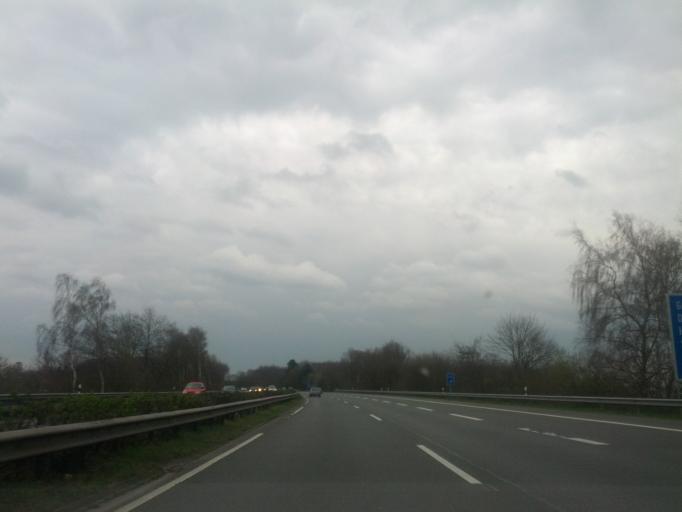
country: DE
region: Lower Saxony
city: Ganderkesee
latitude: 53.0496
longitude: 8.5496
